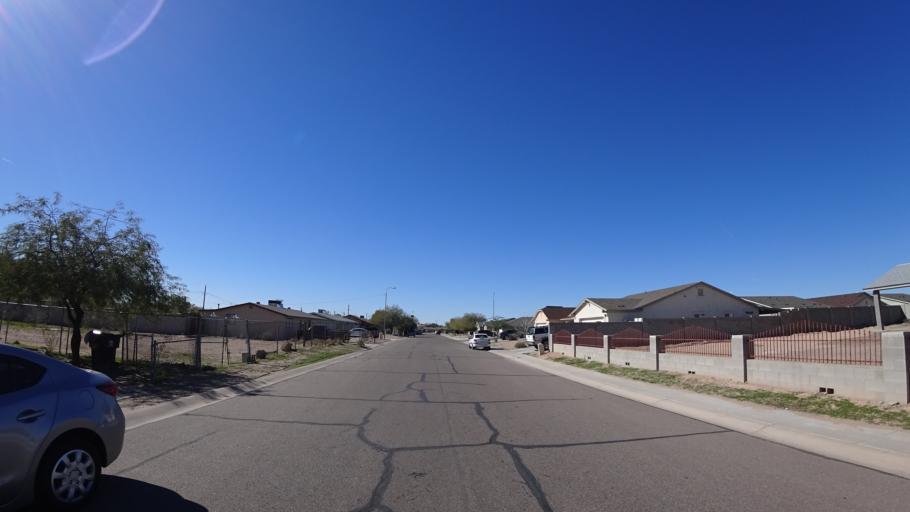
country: US
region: Arizona
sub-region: Maricopa County
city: Avondale
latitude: 33.4143
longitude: -112.3297
